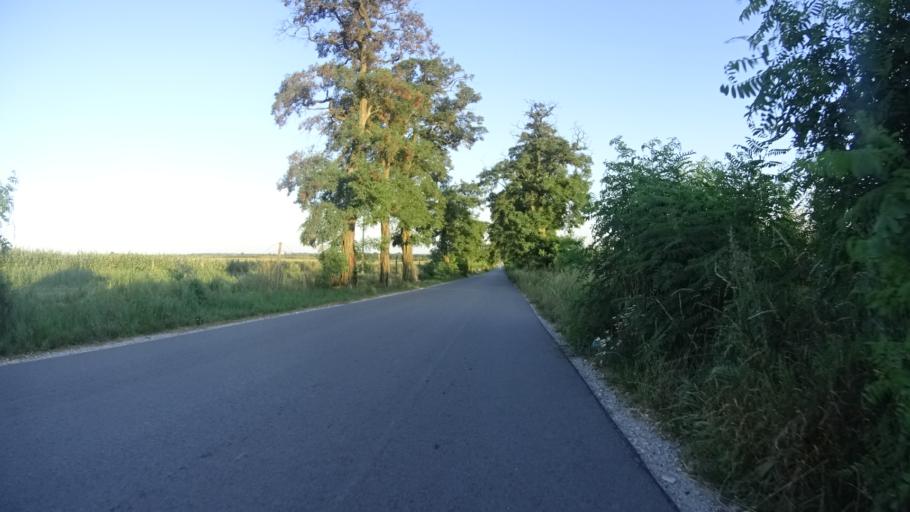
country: PL
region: Masovian Voivodeship
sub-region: Powiat grojecki
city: Goszczyn
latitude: 51.6874
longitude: 20.8204
